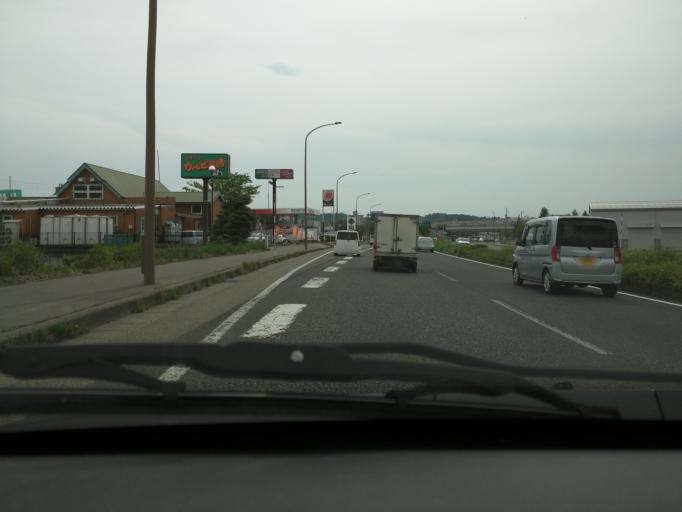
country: JP
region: Niigata
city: Nagaoka
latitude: 37.4463
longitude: 138.7966
